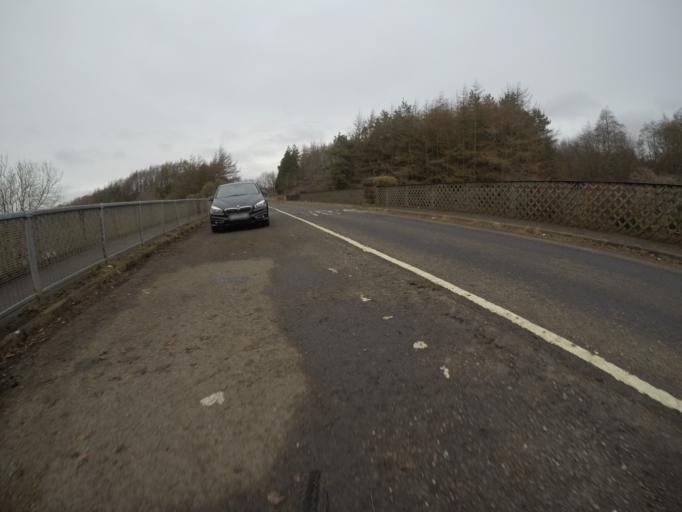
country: GB
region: Scotland
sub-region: North Ayrshire
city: Kilwinning
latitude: 55.6401
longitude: -4.6909
